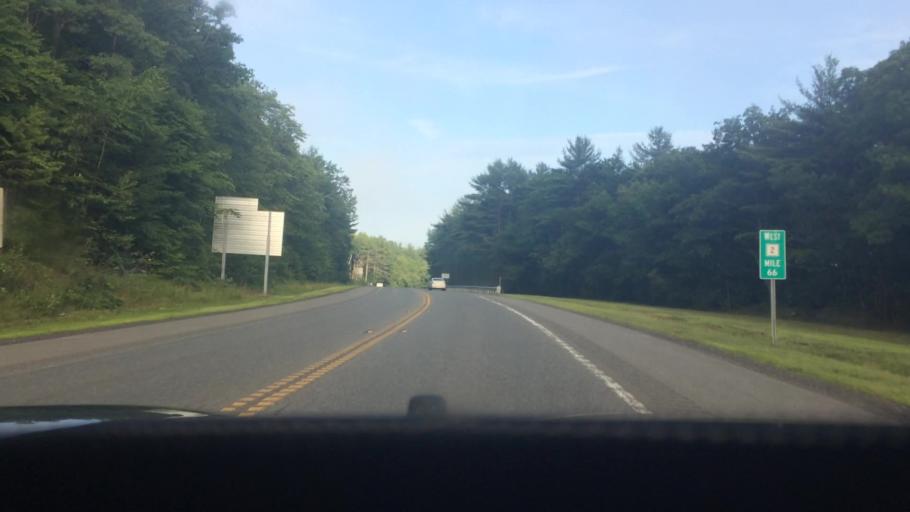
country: US
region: Massachusetts
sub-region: Franklin County
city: Orange
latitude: 42.5970
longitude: -72.3477
